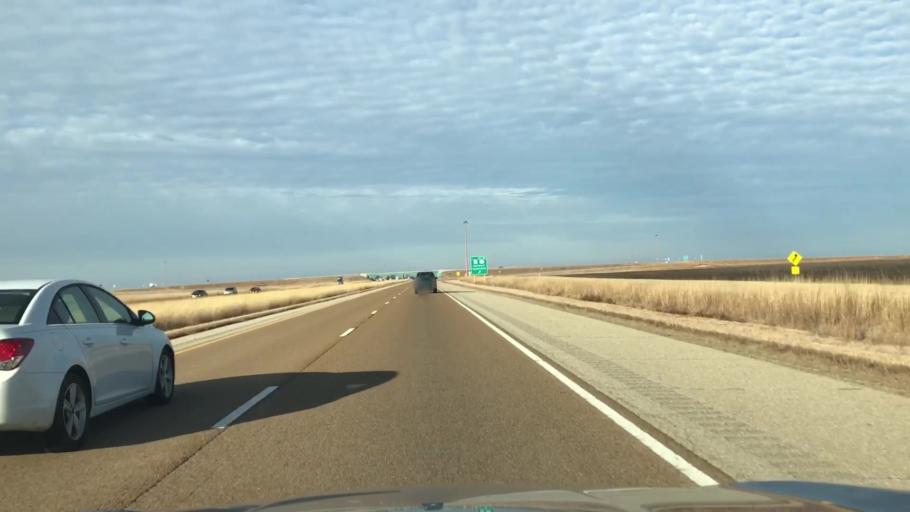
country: US
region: Illinois
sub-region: Montgomery County
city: Raymond
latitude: 39.3147
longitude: -89.6423
